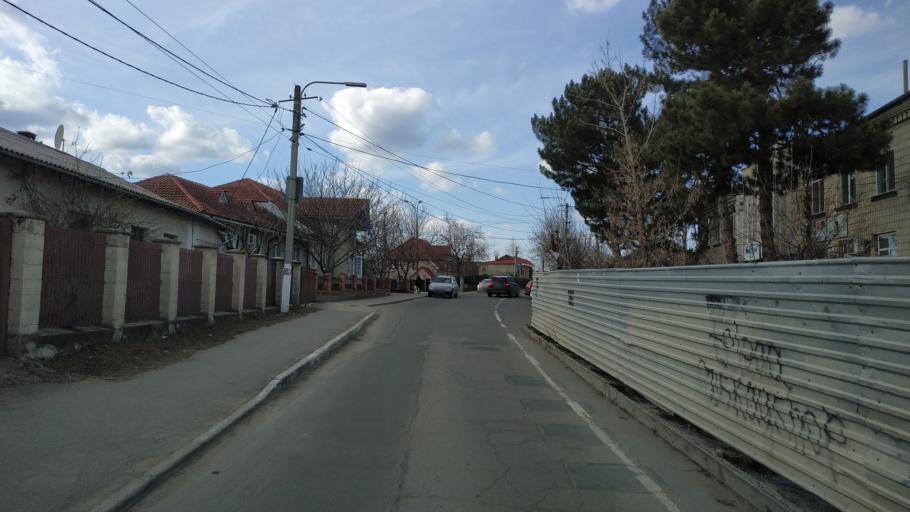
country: MD
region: Hincesti
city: Hincesti
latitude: 46.8287
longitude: 28.5878
